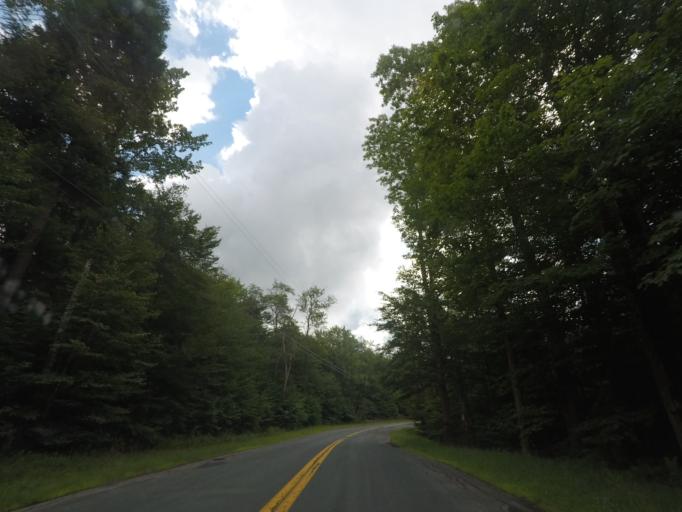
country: US
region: New York
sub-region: Rensselaer County
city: Averill Park
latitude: 42.6659
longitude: -73.4162
